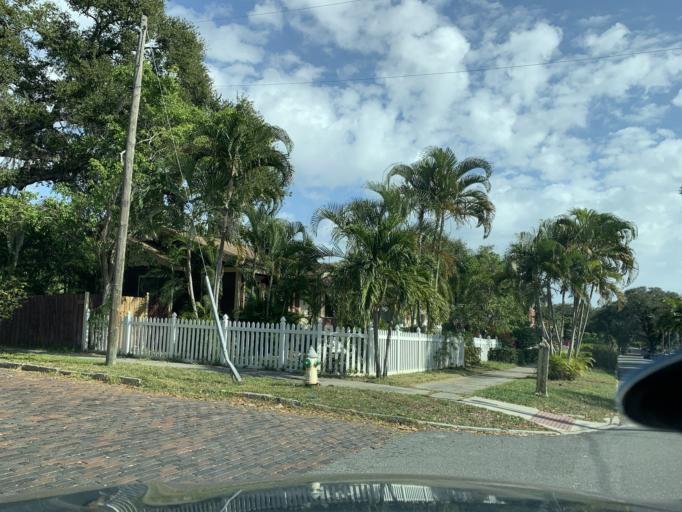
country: US
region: Florida
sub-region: Pinellas County
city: Saint Petersburg
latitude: 27.7585
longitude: -82.6435
